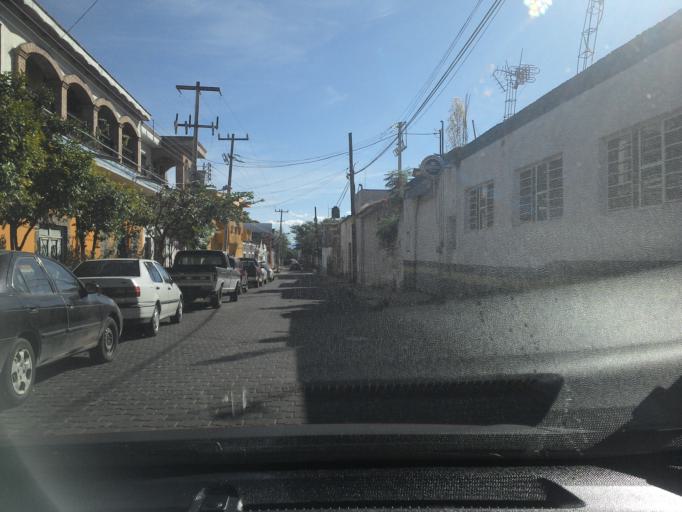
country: MX
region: Jalisco
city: Teuchitlan
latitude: 20.6832
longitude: -103.8471
